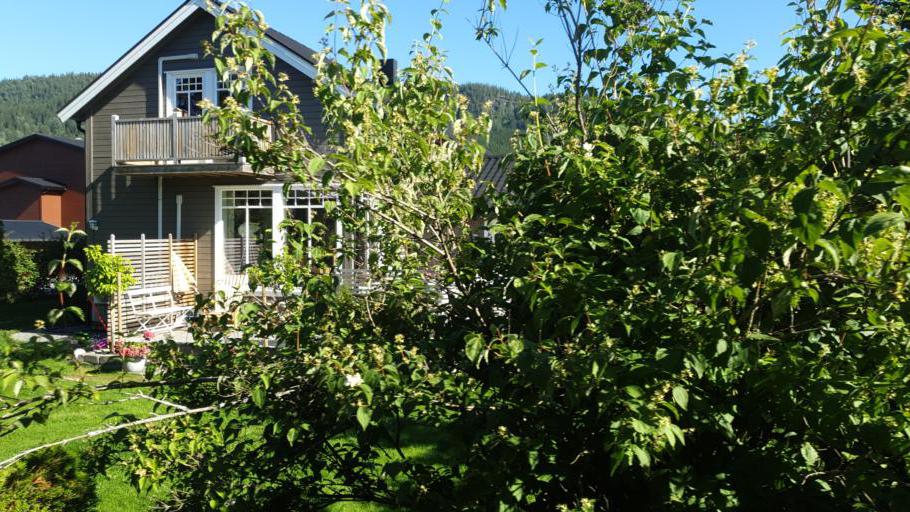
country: NO
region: Sor-Trondelag
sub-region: Orkdal
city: Orkanger
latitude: 63.2763
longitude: 9.8243
